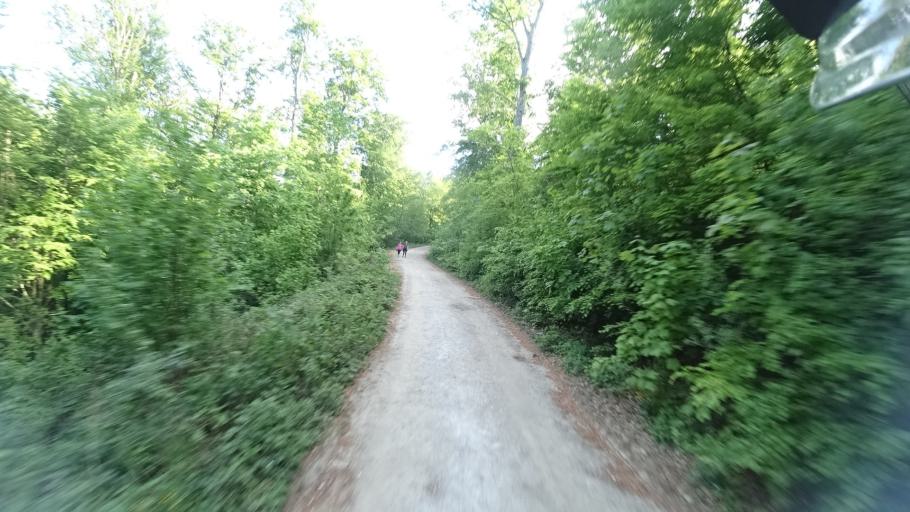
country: HR
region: Zagrebacka
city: Jablanovec
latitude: 45.8531
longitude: 15.8902
